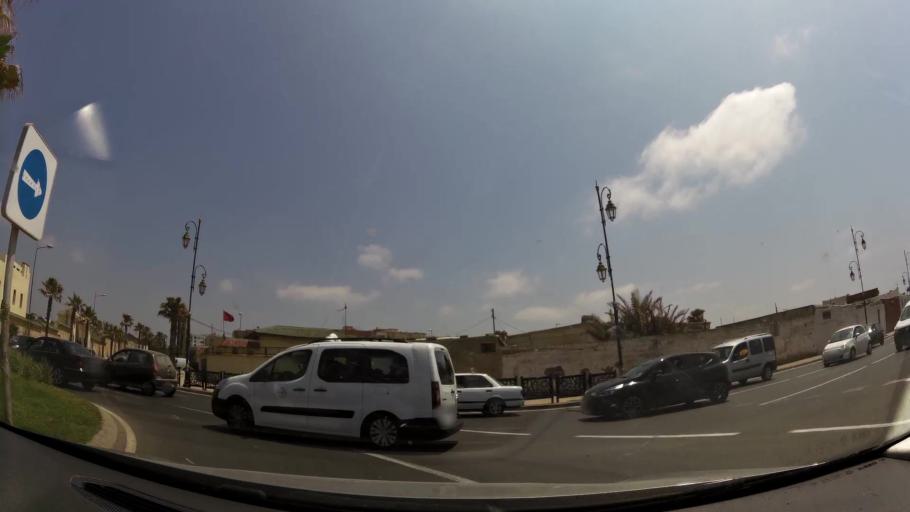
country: MA
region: Rabat-Sale-Zemmour-Zaer
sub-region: Rabat
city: Rabat
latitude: 34.0182
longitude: -6.8575
